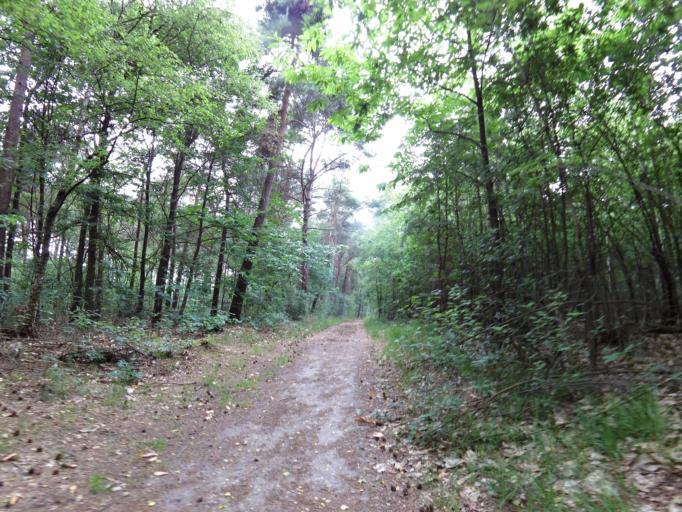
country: NL
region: North Brabant
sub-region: Gemeente Cuijk
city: Cuijk
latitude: 51.7672
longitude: 5.8839
